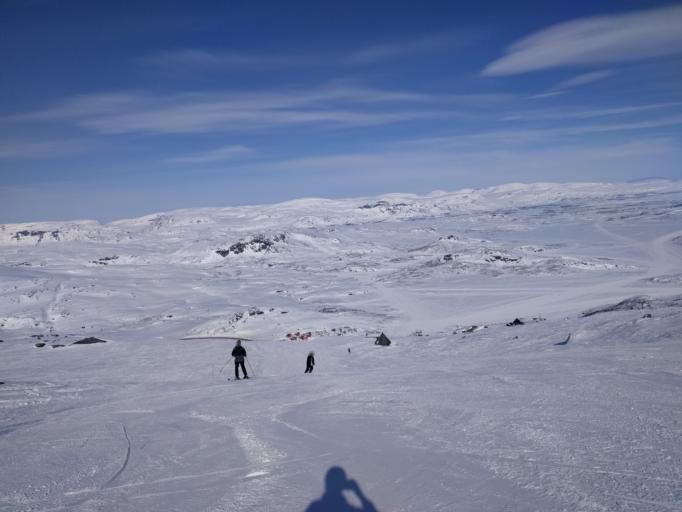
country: NO
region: Troms
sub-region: Lavangen
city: Tennevoll
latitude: 68.4197
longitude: 18.1019
